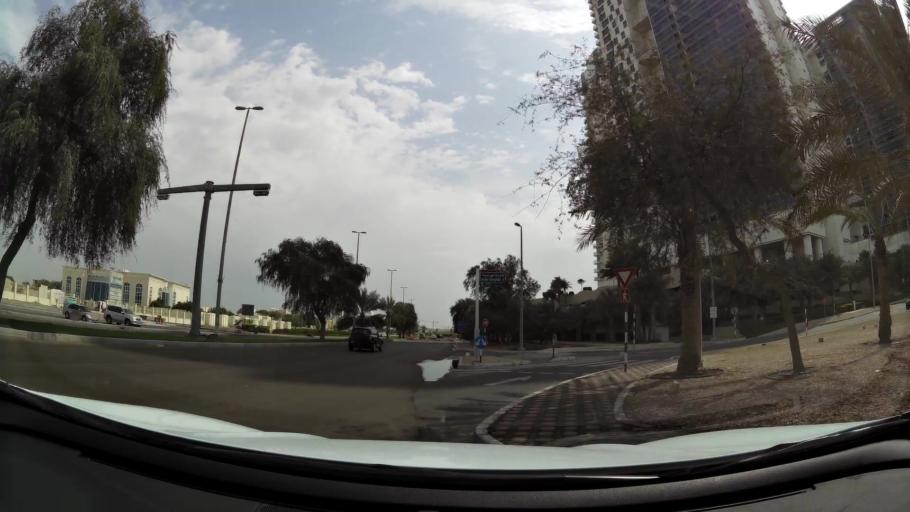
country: AE
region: Abu Dhabi
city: Abu Dhabi
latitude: 24.4153
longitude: 54.4625
